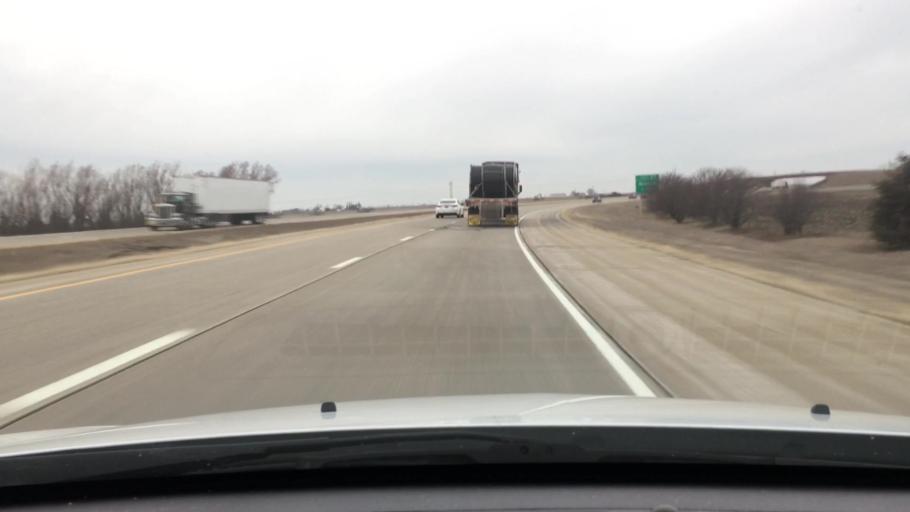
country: US
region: Illinois
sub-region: Woodford County
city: Minonk
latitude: 40.8934
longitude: -89.0496
